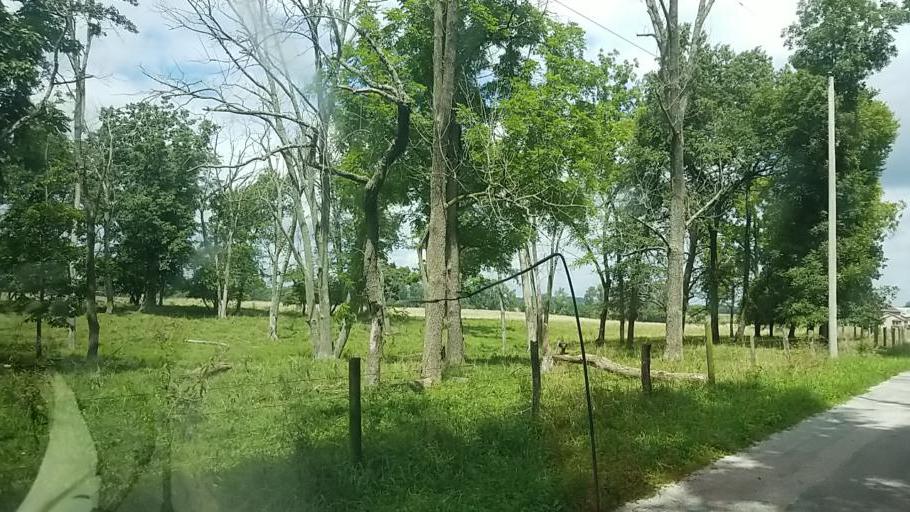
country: US
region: Ohio
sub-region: Clark County
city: South Charleston
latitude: 39.8186
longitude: -83.7212
